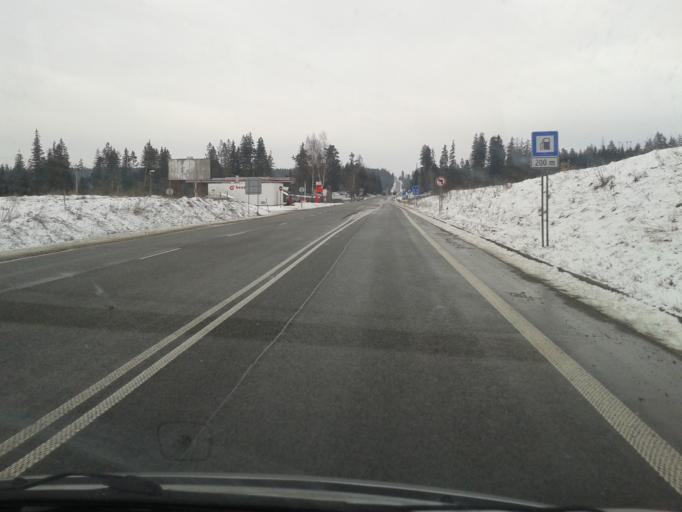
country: PL
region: Lesser Poland Voivodeship
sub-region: Powiat nowotarski
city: Chyzne
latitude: 49.3997
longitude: 19.6501
